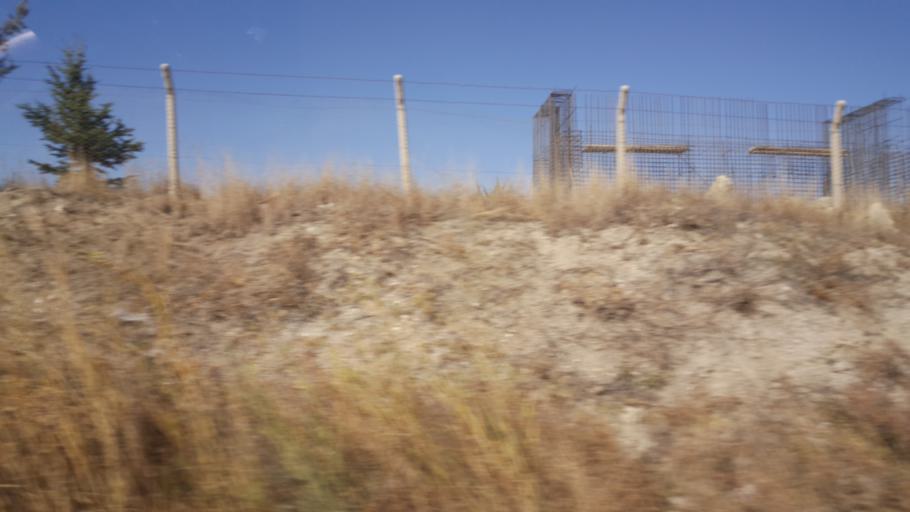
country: TR
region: Ankara
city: Ikizce
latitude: 39.6591
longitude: 32.7302
